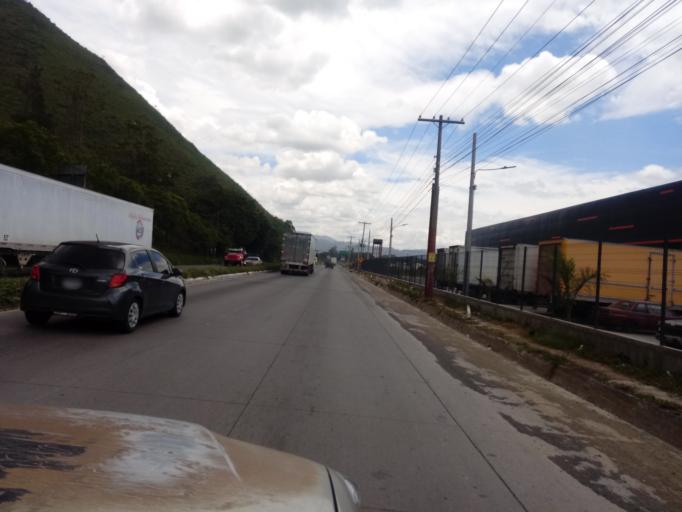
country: GT
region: Escuintla
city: San Vicente Pacaya
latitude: 14.4525
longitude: -90.6436
